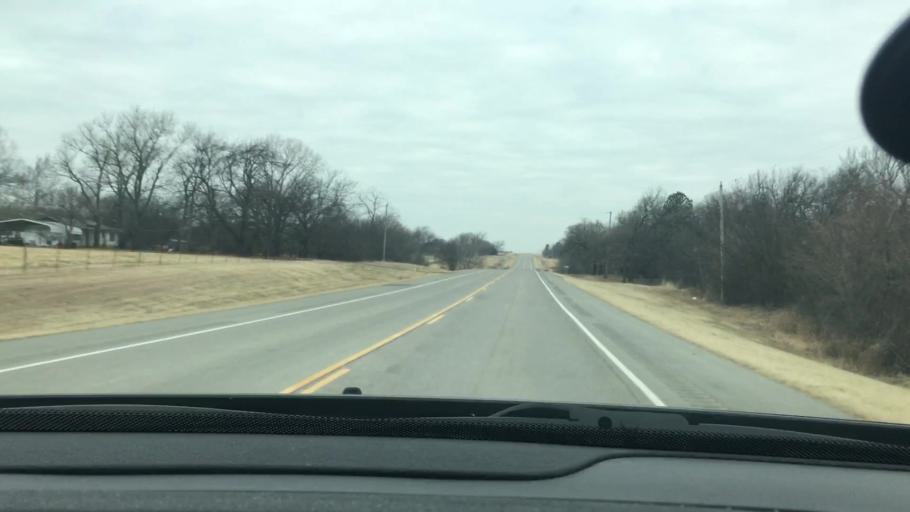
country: US
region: Oklahoma
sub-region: Murray County
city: Davis
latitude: 34.4925
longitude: -97.3775
